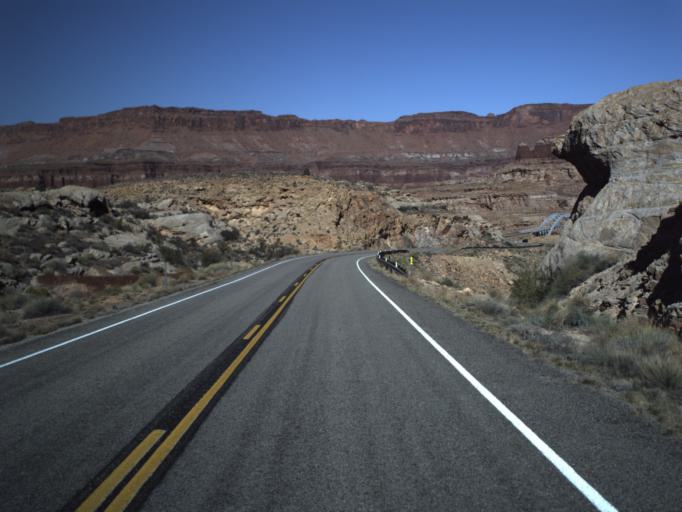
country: US
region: Utah
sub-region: San Juan County
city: Blanding
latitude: 37.8852
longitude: -110.3638
